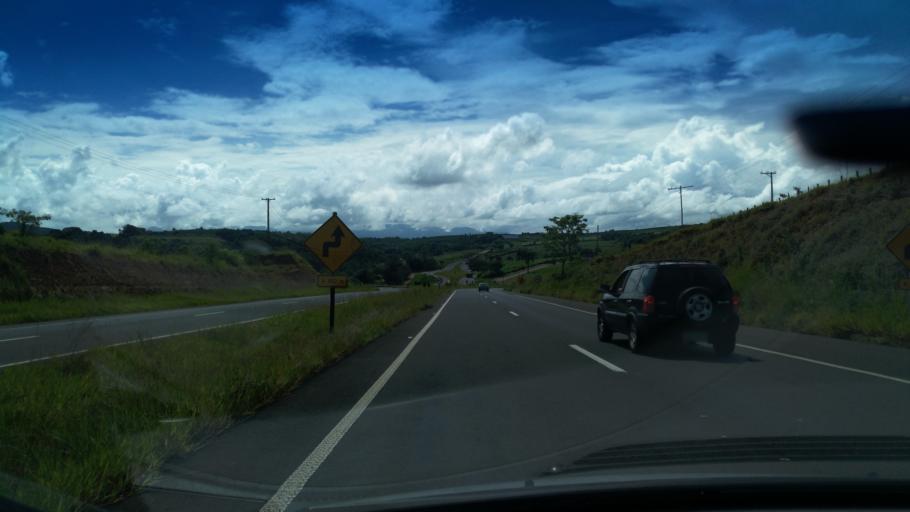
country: BR
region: Sao Paulo
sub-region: Santo Antonio Do Jardim
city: Espirito Santo do Pinhal
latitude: -22.1691
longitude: -46.7414
